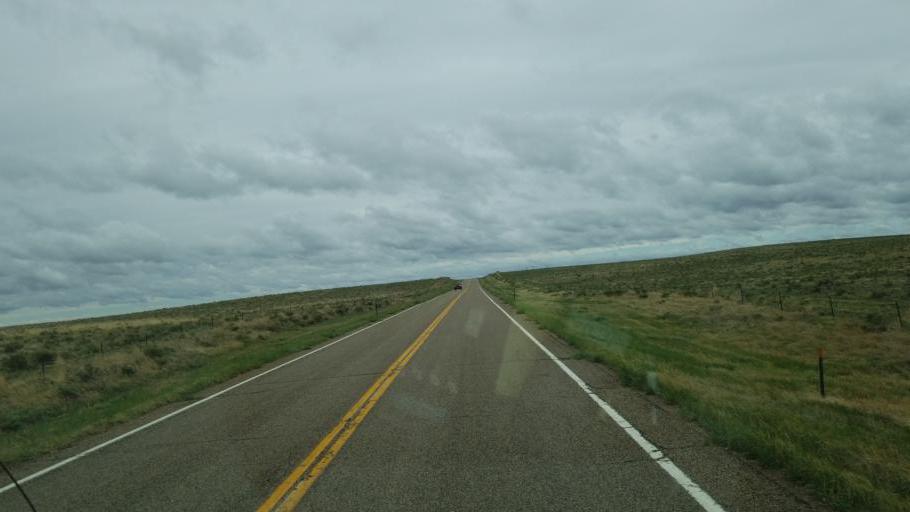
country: US
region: Colorado
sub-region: Lincoln County
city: Hugo
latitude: 38.8502
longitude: -103.5102
